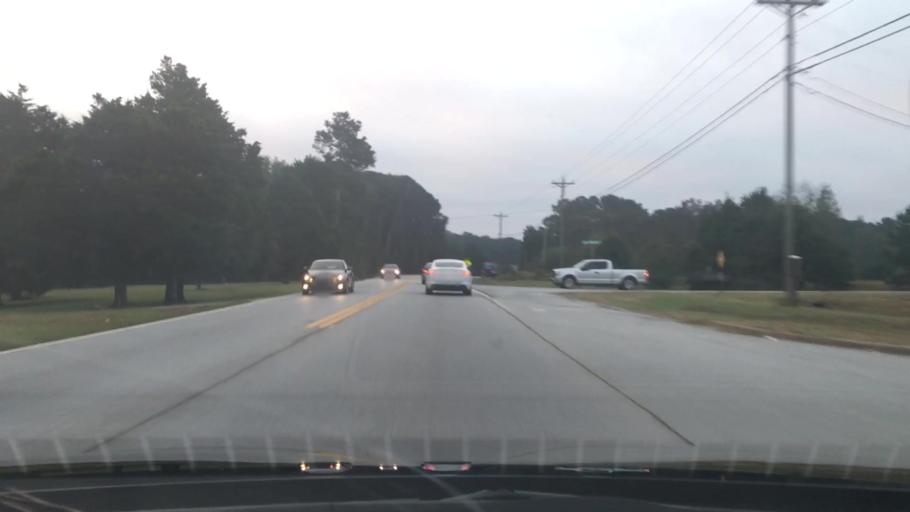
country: US
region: Georgia
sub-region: Fayette County
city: Peachtree City
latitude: 33.3714
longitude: -84.6651
